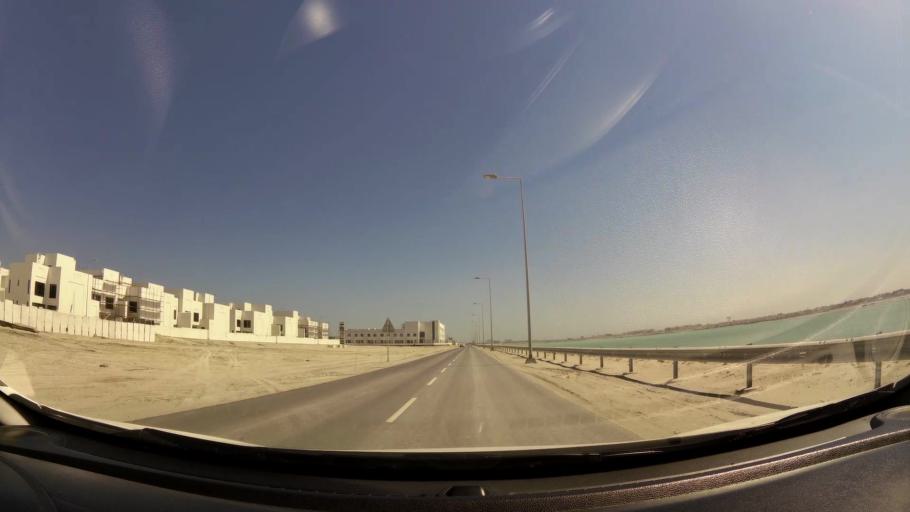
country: BH
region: Muharraq
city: Al Muharraq
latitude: 26.2996
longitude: 50.6333
